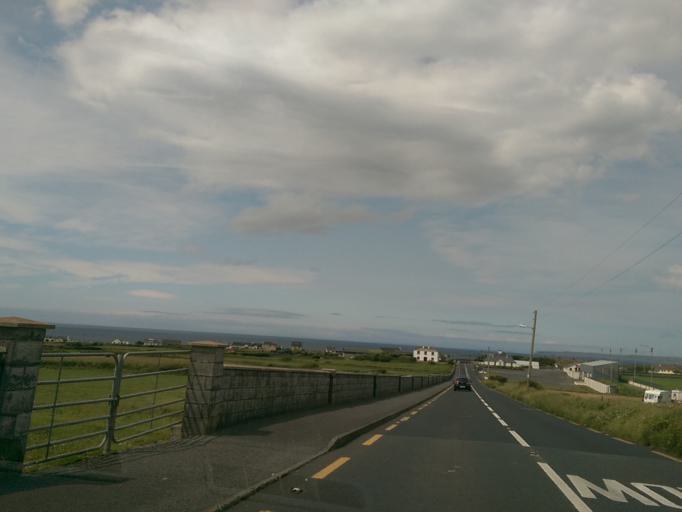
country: IE
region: Munster
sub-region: An Clar
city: Kilrush
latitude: 52.8118
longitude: -9.4548
